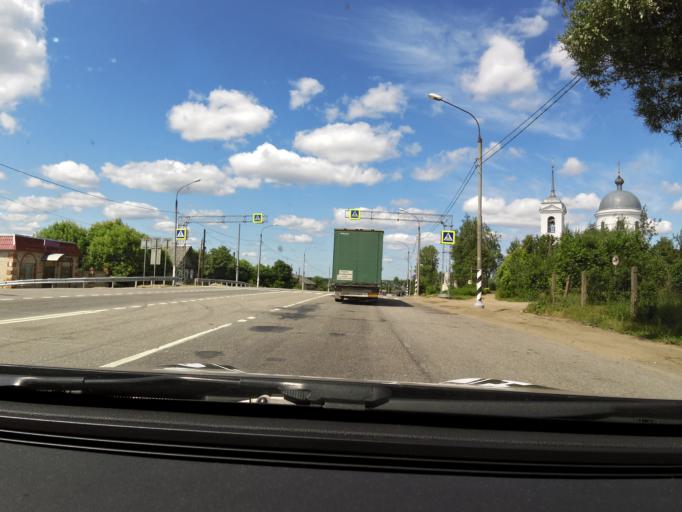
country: RU
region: Tverskaya
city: Kuzhenkino
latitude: 57.7606
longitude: 33.9543
